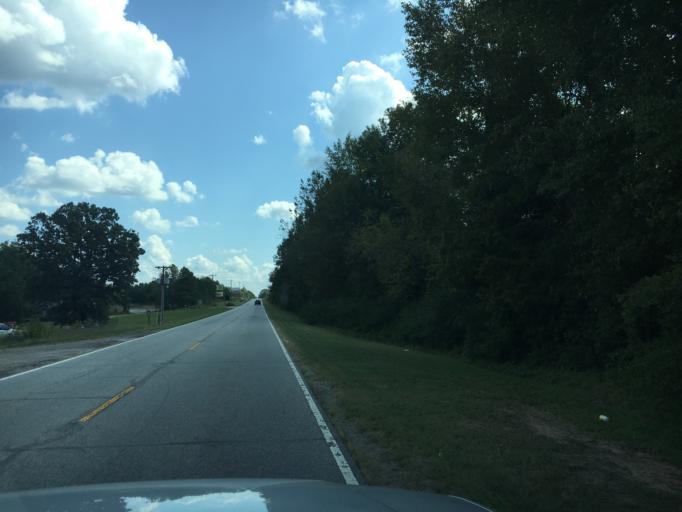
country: US
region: South Carolina
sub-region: Greenville County
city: Fountain Inn
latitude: 34.6003
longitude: -82.1084
